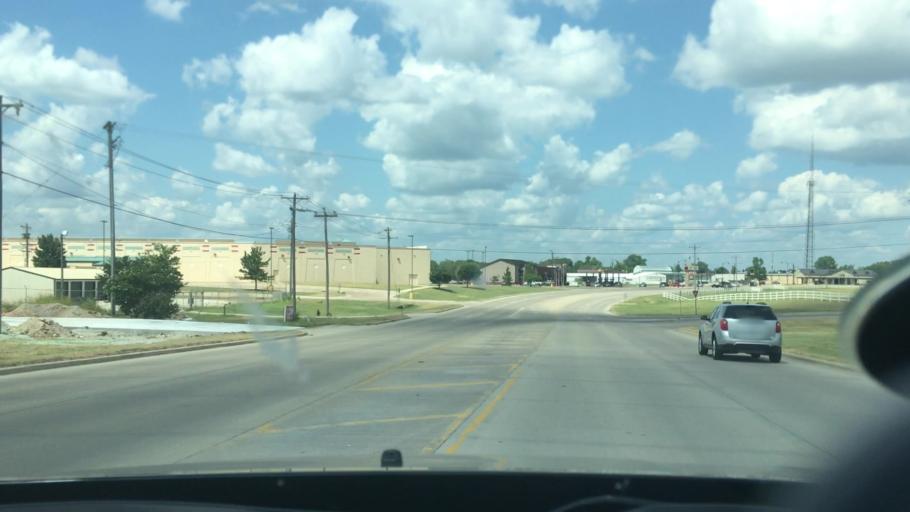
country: US
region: Oklahoma
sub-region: Pontotoc County
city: Ada
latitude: 34.7706
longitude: -96.6989
